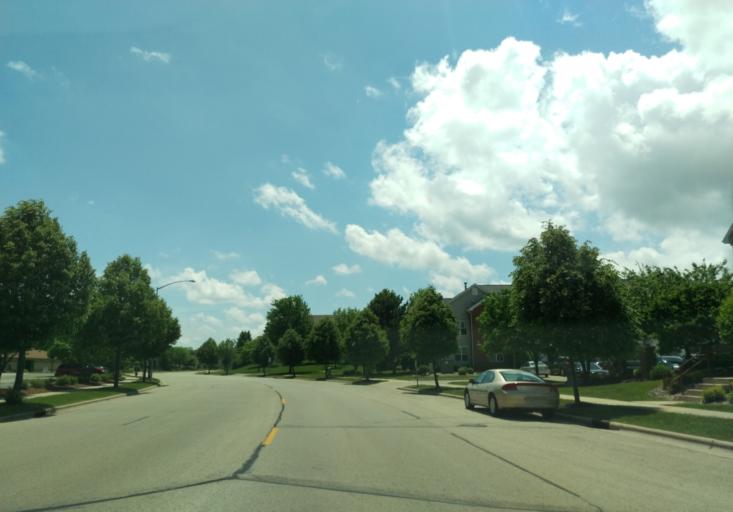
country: US
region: Wisconsin
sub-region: Dane County
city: Middleton
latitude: 43.0802
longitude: -89.5194
